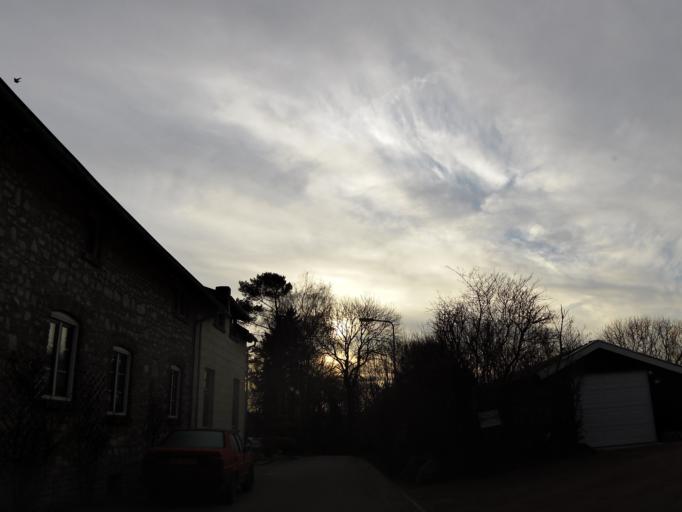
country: NL
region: Limburg
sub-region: Gemeente Voerendaal
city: Ubachsberg
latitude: 50.8405
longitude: 5.9198
